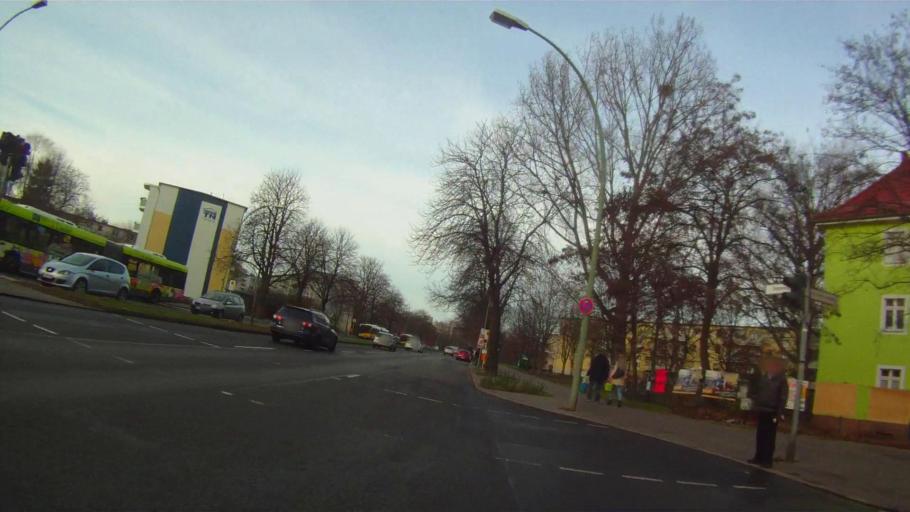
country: DE
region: Berlin
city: Baumschulenweg
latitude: 52.4610
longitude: 13.4809
